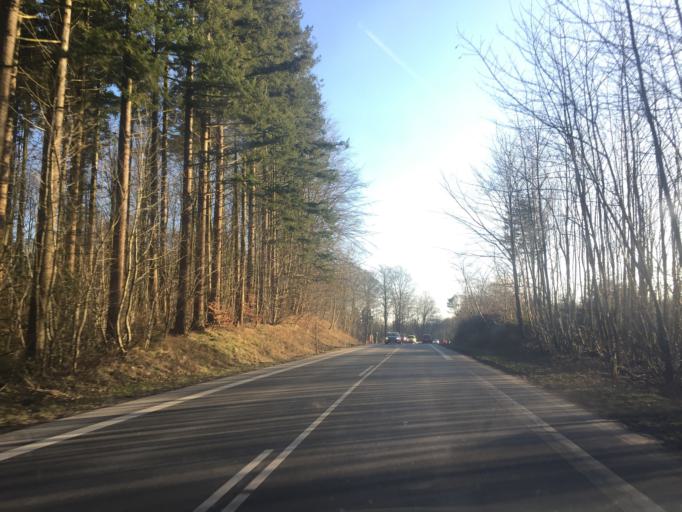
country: DK
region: South Denmark
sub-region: Assens Kommune
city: Vissenbjerg
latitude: 55.4345
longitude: 10.1839
